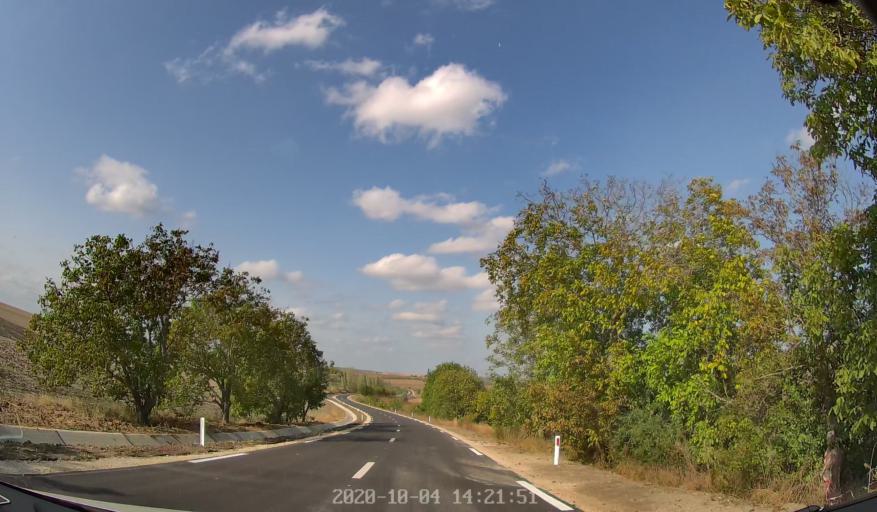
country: MD
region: Rezina
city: Saharna
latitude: 47.5902
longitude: 28.9530
